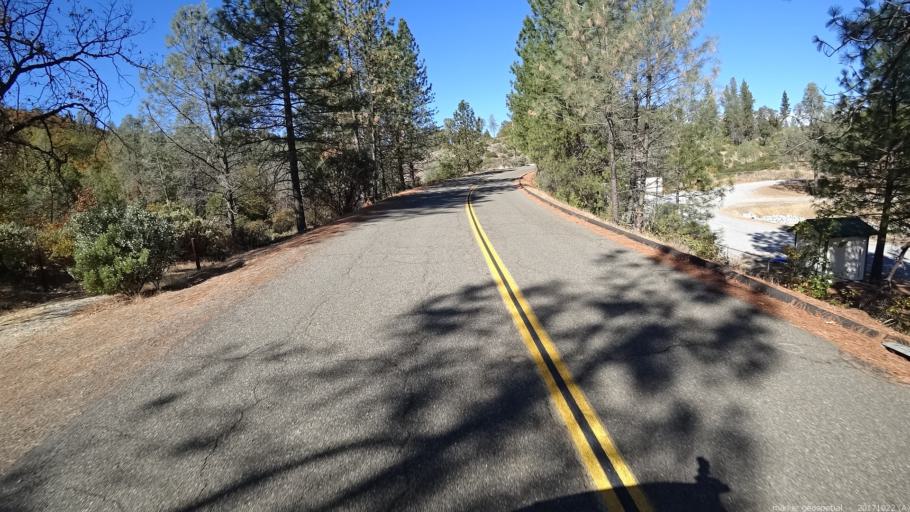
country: US
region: California
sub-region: Shasta County
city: Central Valley (historical)
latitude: 40.8944
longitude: -122.3862
